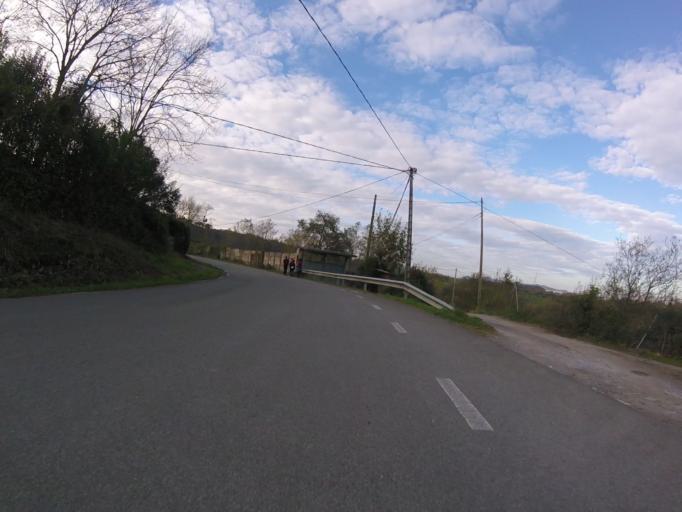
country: ES
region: Basque Country
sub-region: Provincia de Guipuzcoa
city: Errenteria
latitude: 43.3072
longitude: -1.9201
